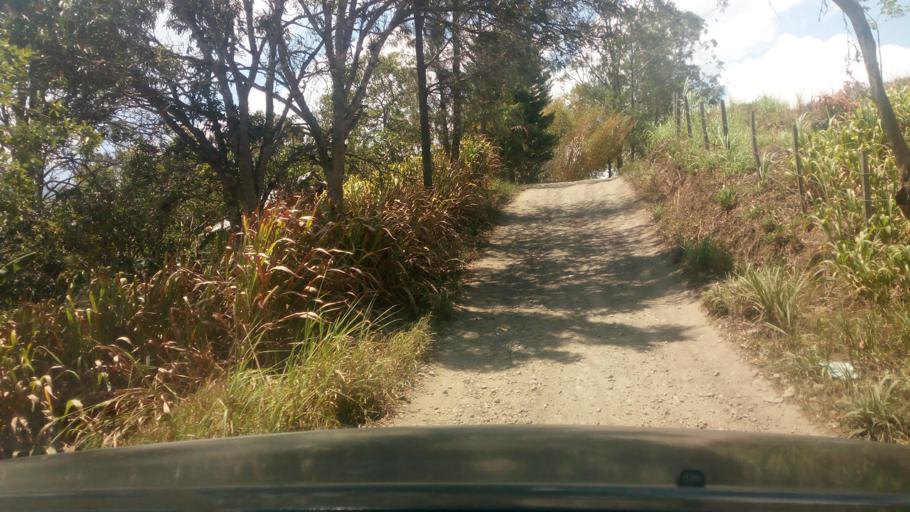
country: CO
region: Boyaca
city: Guateque
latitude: 4.9899
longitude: -73.4647
